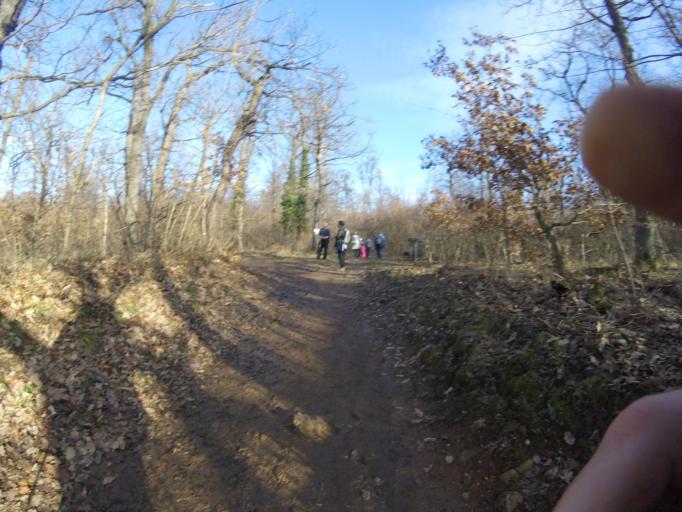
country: HU
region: Pest
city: Budakeszi
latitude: 47.5326
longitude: 18.9532
